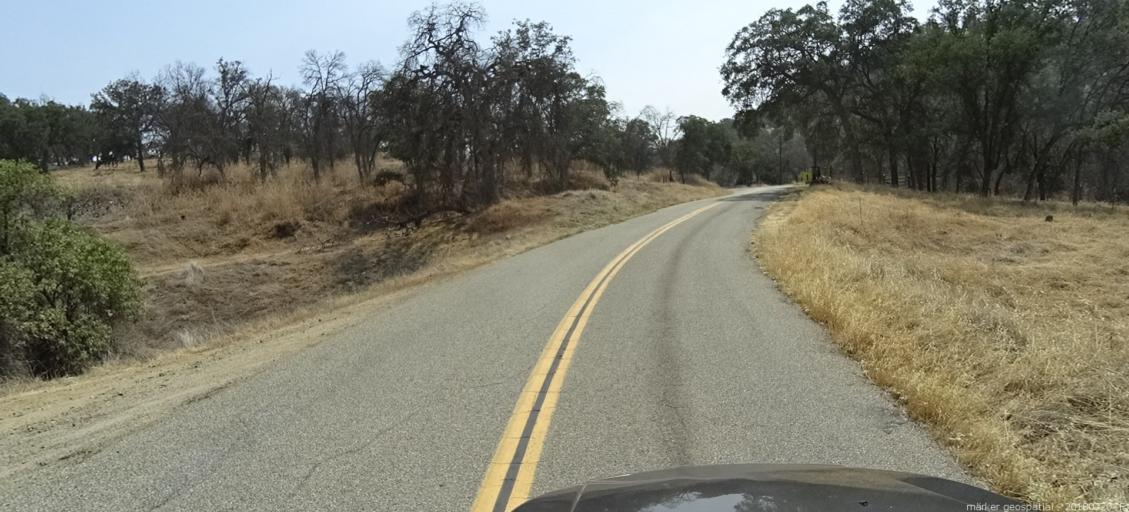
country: US
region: California
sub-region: Madera County
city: Ahwahnee
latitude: 37.3223
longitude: -119.7797
